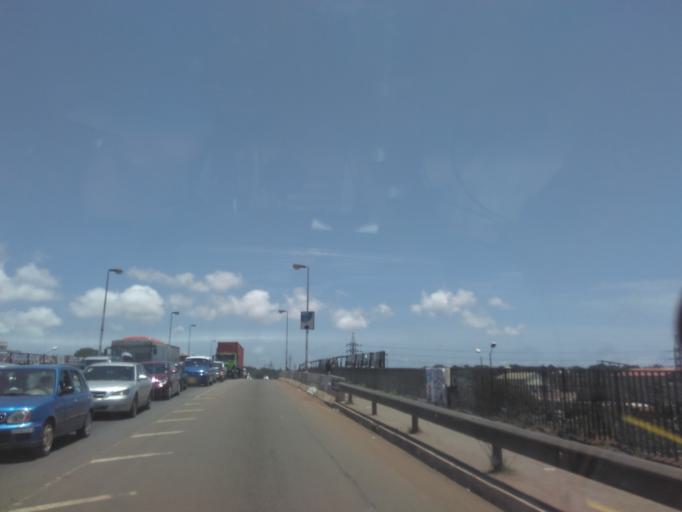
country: GH
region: Greater Accra
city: Tema
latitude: 5.6827
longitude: -0.0260
